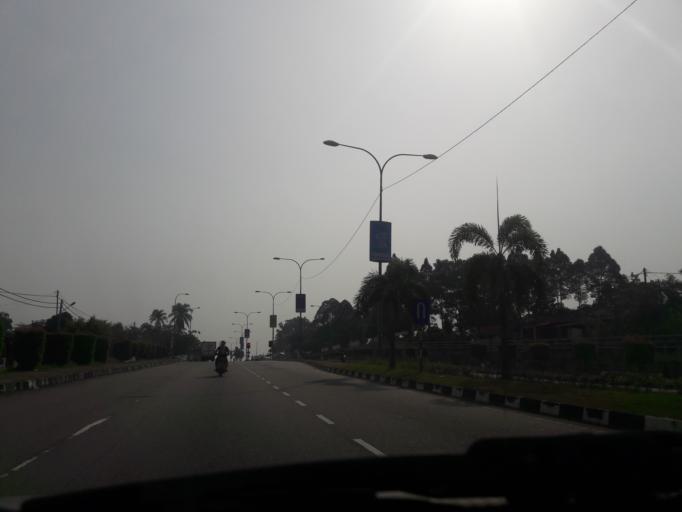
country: MY
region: Kedah
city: Kulim
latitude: 5.3586
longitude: 100.5437
